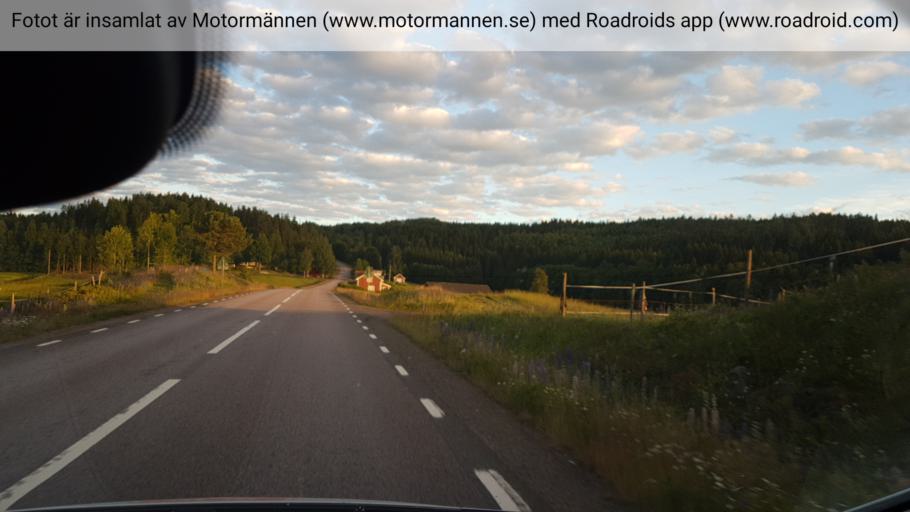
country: SE
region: Vaermland
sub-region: Sunne Kommun
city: Sunne
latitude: 59.7145
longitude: 13.1042
